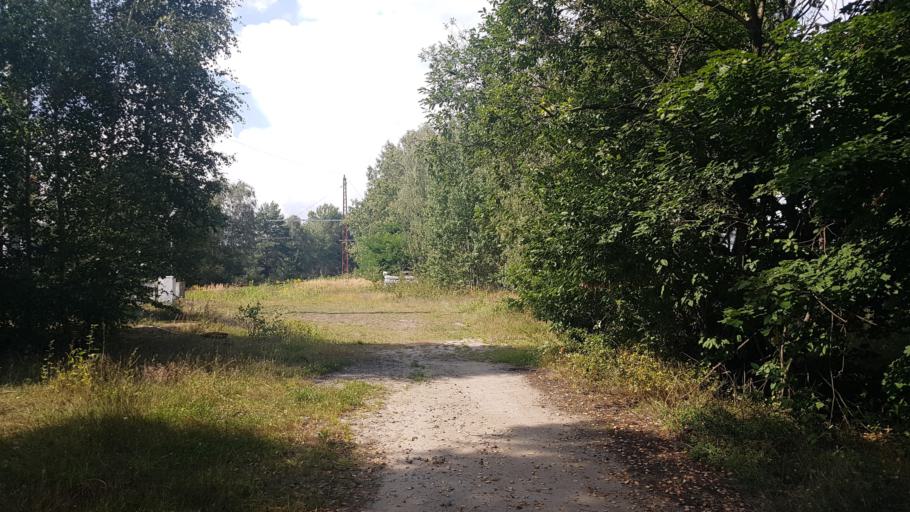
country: DE
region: Brandenburg
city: Bronkow
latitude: 51.6519
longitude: 13.8863
